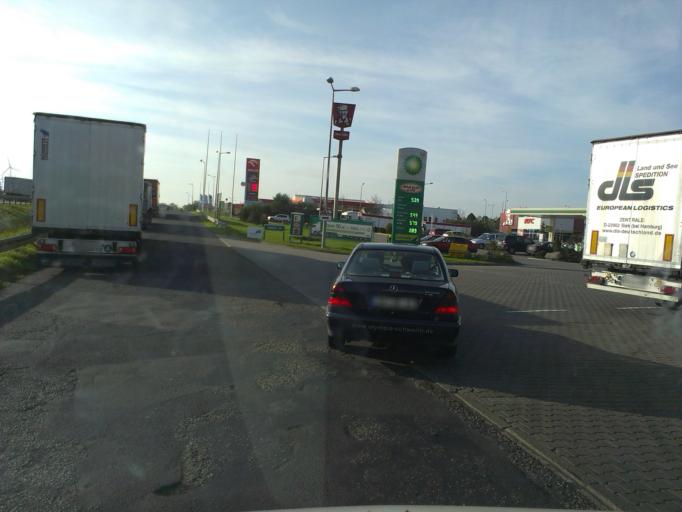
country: PL
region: West Pomeranian Voivodeship
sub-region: Powiat policki
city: Kolbaskowo
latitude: 53.3384
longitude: 14.4262
